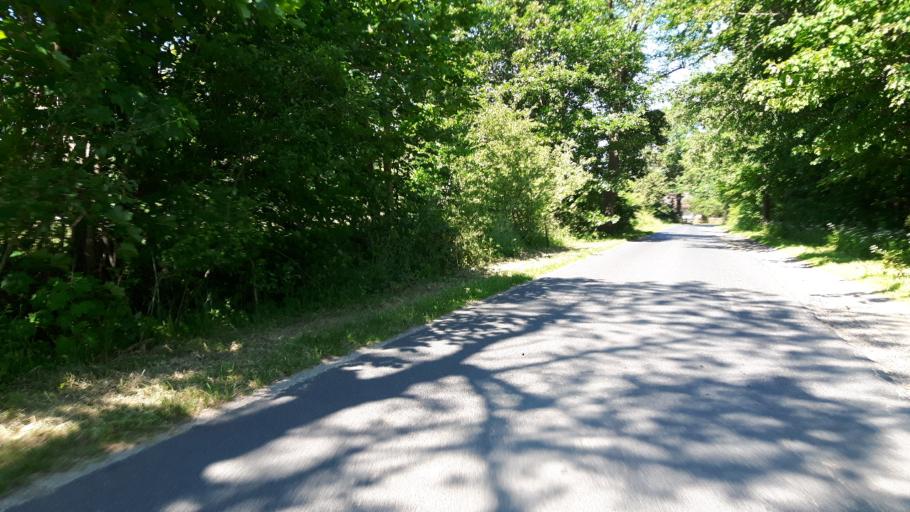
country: PL
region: Pomeranian Voivodeship
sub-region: Powiat slupski
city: Glowczyce
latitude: 54.6386
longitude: 17.4095
